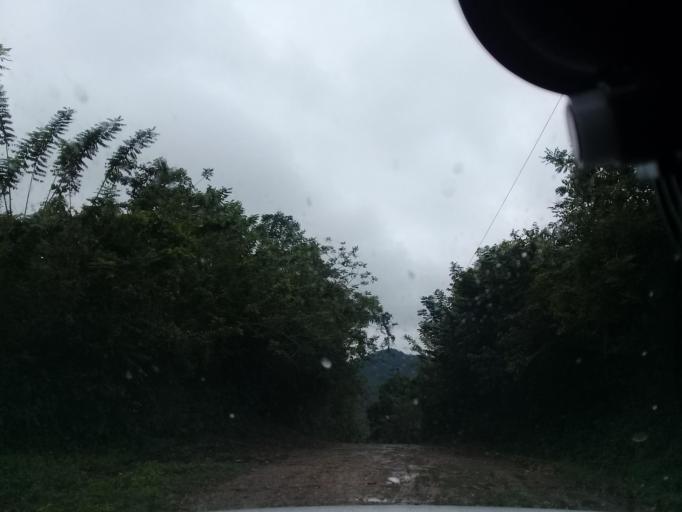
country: MX
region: Veracruz
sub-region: Chalma
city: San Pedro Coyutla
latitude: 21.2364
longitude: -98.4387
